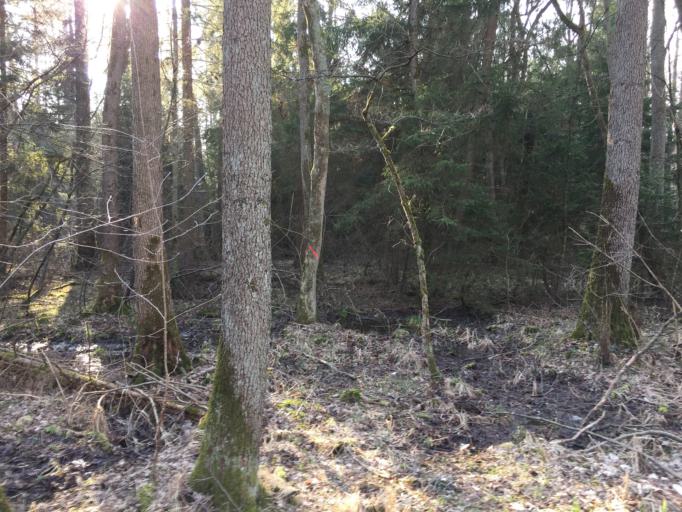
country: DE
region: Bavaria
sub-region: Regierungsbezirk Mittelfranken
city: Erlangen
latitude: 49.5642
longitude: 11.0217
